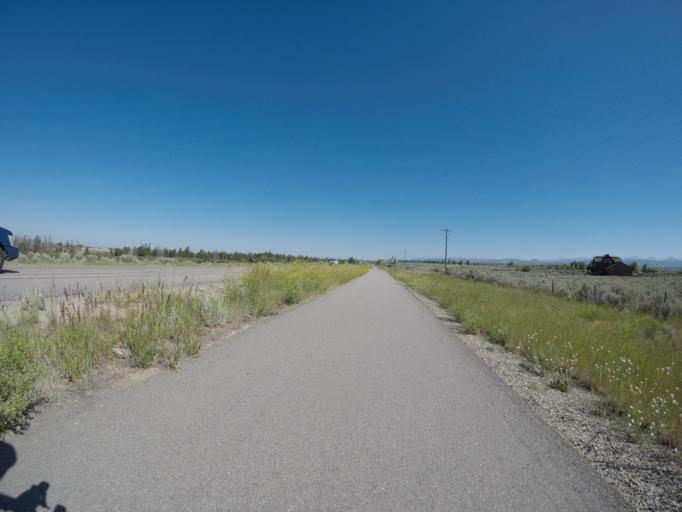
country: US
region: Wyoming
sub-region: Sublette County
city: Pinedale
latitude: 42.8446
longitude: -109.8473
